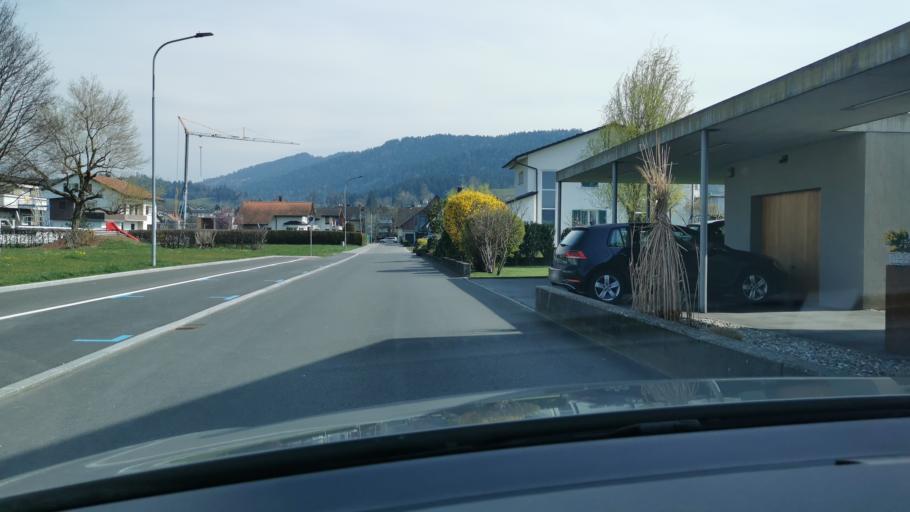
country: AT
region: Vorarlberg
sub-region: Politischer Bezirk Bregenz
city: Wolfurt
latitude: 47.4759
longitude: 9.7483
